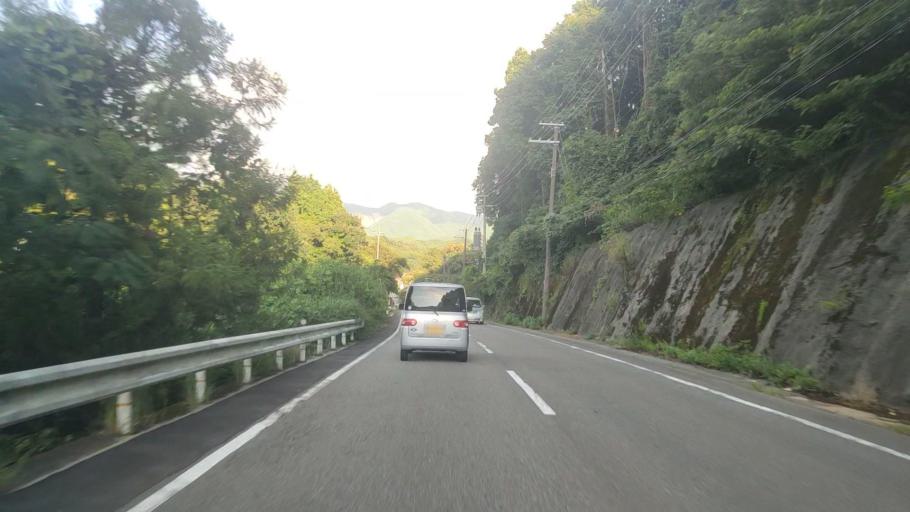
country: JP
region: Wakayama
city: Tanabe
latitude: 33.7275
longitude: 135.4378
